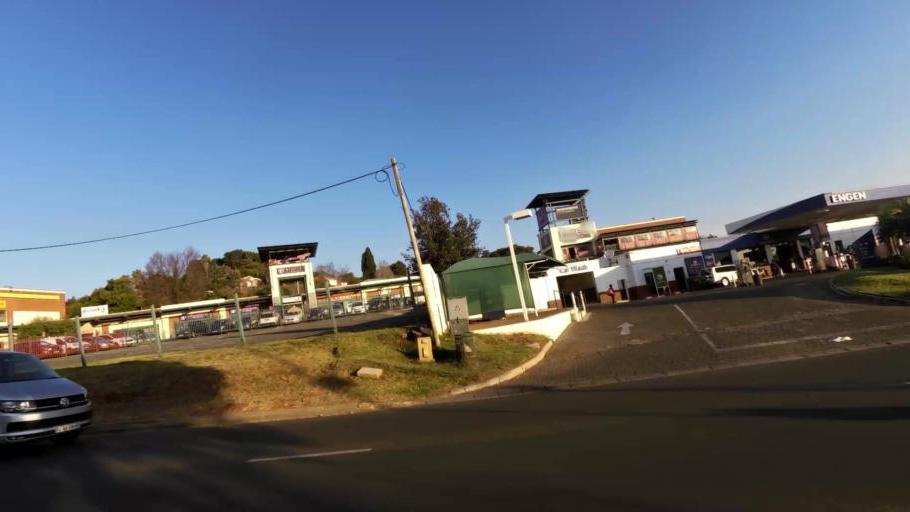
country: ZA
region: Gauteng
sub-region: City of Johannesburg Metropolitan Municipality
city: Roodepoort
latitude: -26.1644
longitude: 27.9445
